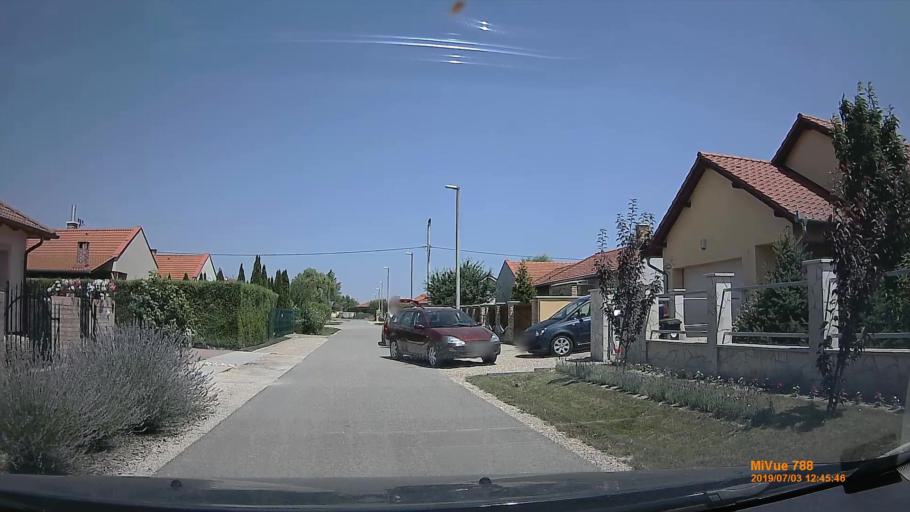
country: HU
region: Gyor-Moson-Sopron
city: Gyor
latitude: 47.7153
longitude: 17.6050
